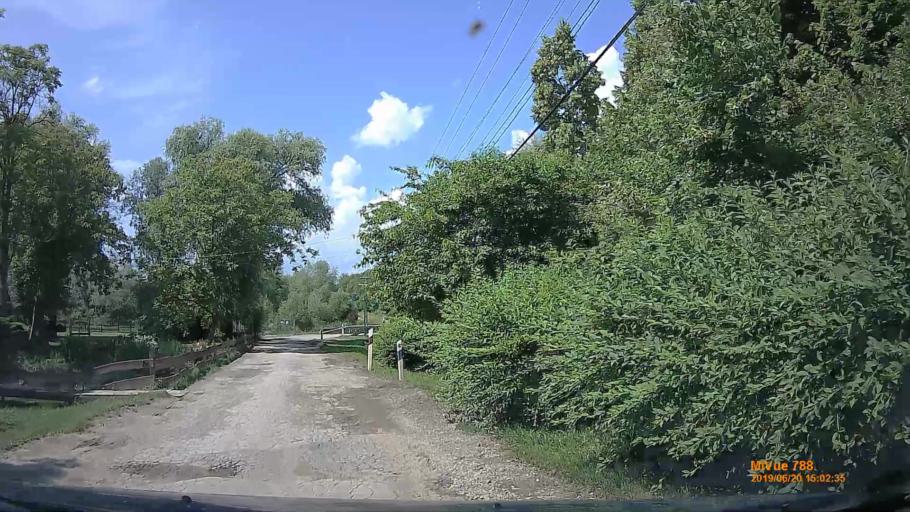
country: HU
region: Baranya
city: Kozarmisleny
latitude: 45.9850
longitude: 18.2629
